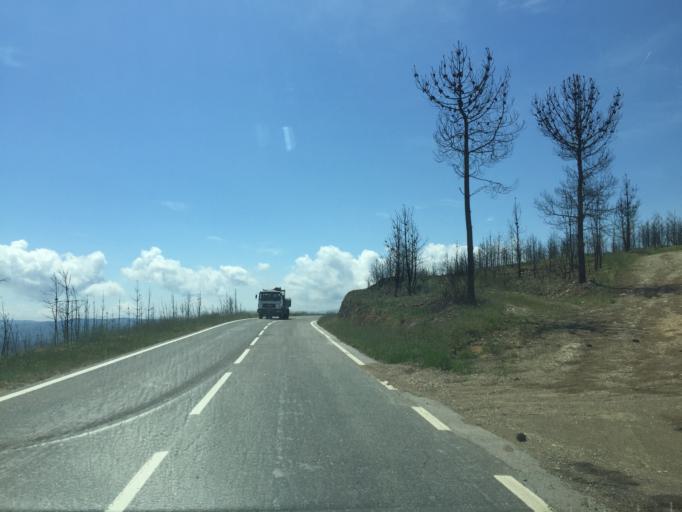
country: PT
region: Coimbra
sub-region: Pampilhosa da Serra
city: Pampilhosa da Serra
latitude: 40.0223
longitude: -7.9645
